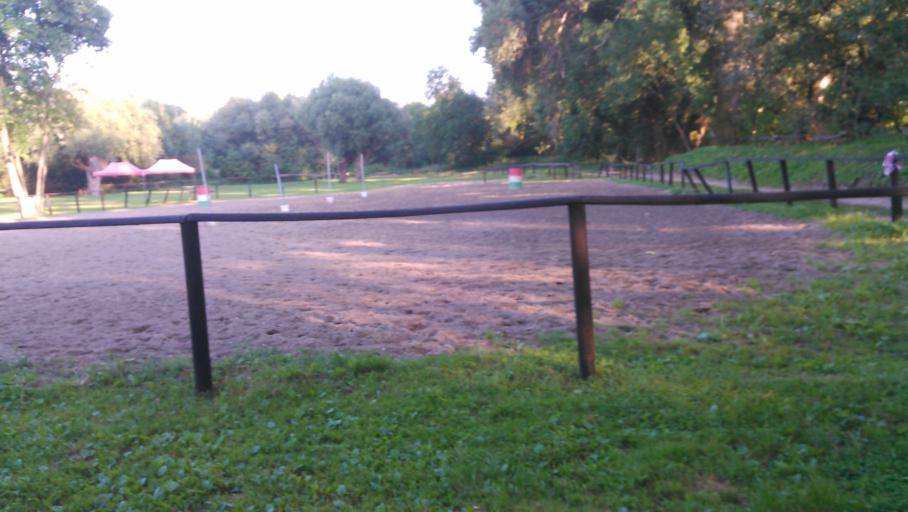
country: SK
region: Nitriansky
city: Kolarovo
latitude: 47.9203
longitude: 18.0029
